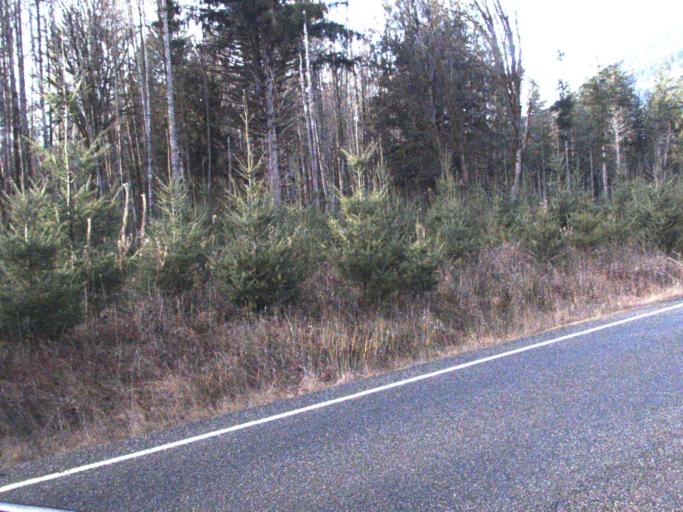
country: US
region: Washington
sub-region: Snohomish County
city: Darrington
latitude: 48.4767
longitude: -121.5906
